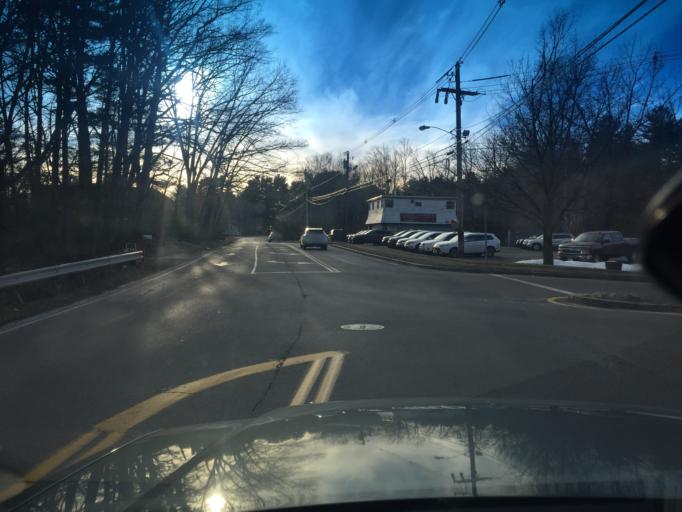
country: US
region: Massachusetts
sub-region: Middlesex County
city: Holliston
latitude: 42.2183
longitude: -71.4105
